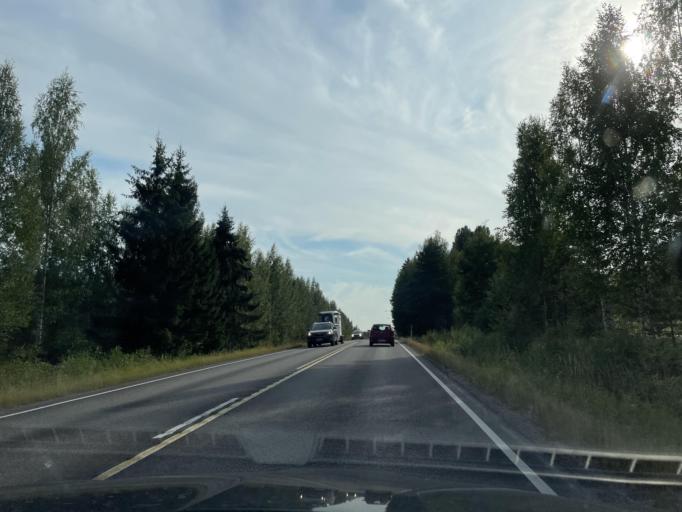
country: FI
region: Central Finland
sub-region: Jaemsae
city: Kuhmoinen
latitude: 61.5888
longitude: 25.2196
